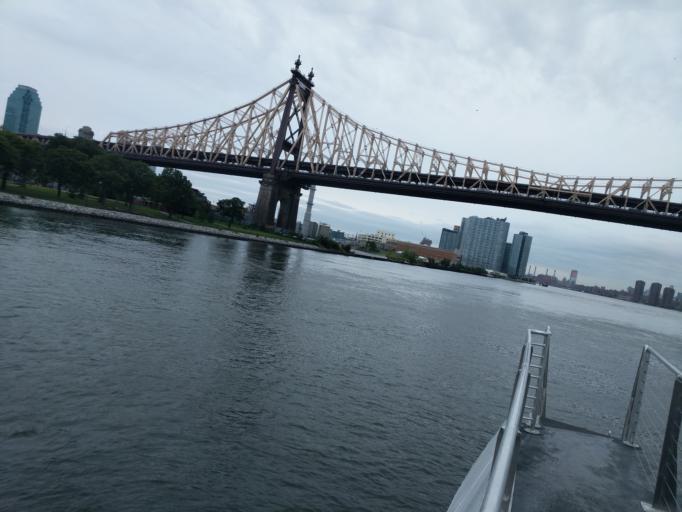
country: US
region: New York
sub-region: Queens County
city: Long Island City
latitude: 40.7578
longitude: -73.9503
